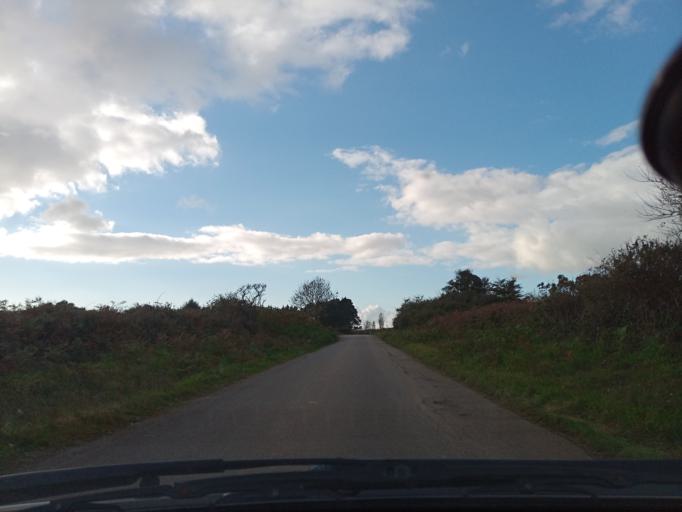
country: FR
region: Brittany
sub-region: Departement du Finistere
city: Plouhinec
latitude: 48.0176
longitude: -4.4961
